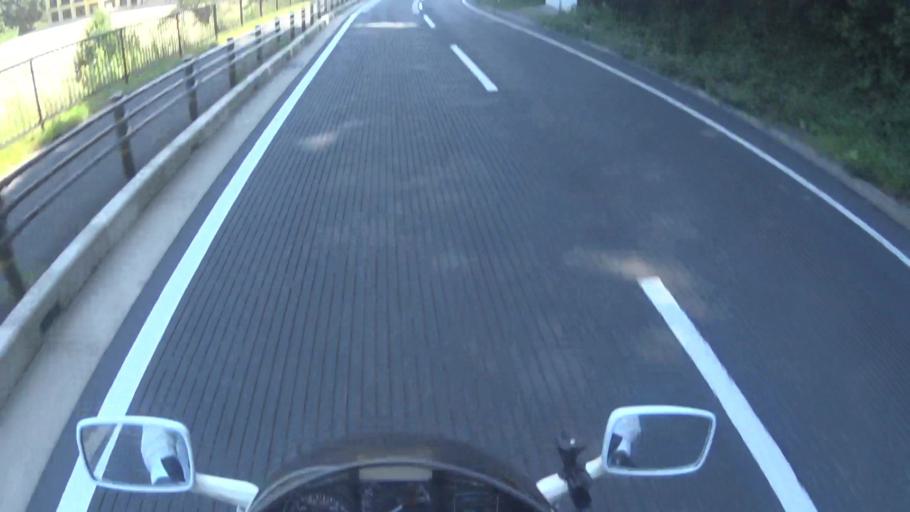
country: JP
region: Kyoto
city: Miyazu
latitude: 35.6790
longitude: 135.2861
